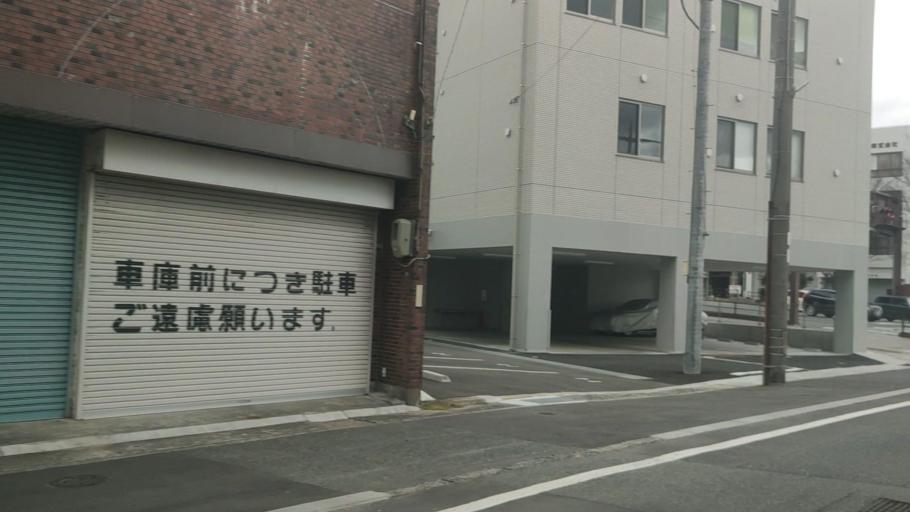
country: JP
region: Yamaguchi
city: Shimonoseki
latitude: 33.9516
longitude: 130.9365
